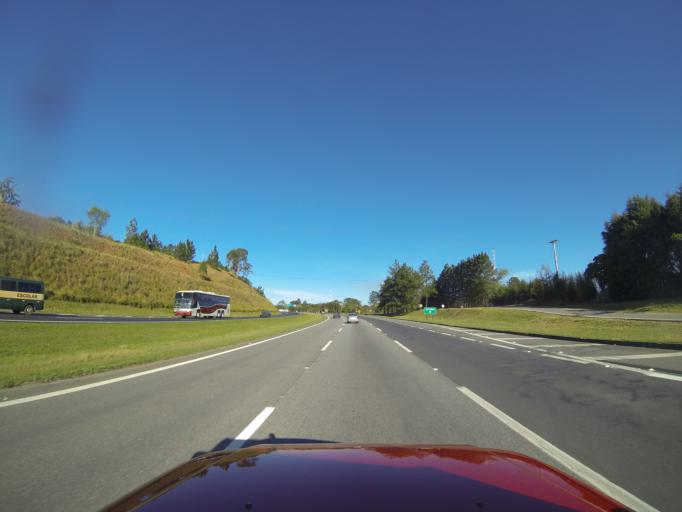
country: BR
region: Sao Paulo
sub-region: Santa Isabel
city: Santa Isabel
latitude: -23.1860
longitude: -46.1995
